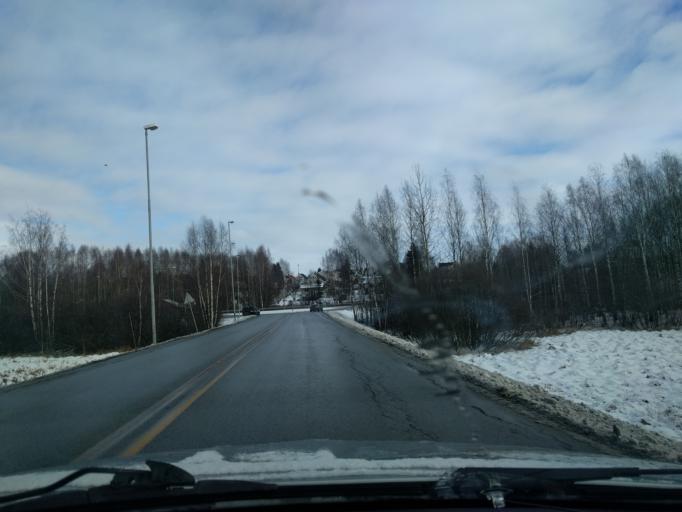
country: NO
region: Hedmark
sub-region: Hamar
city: Hamar
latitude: 60.8003
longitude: 11.1144
